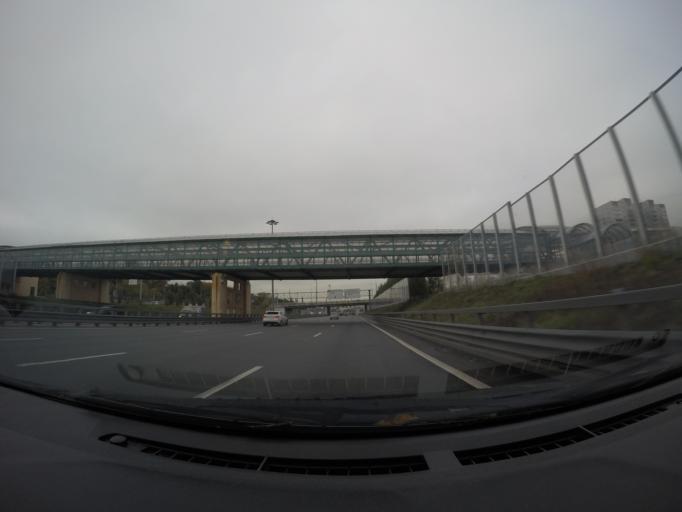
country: RU
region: Moscow
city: Ryazanskiy
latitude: 55.7705
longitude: 37.7465
